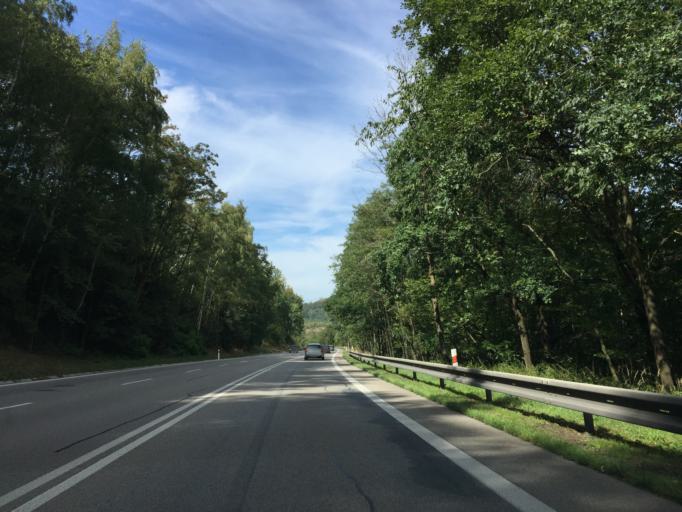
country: CZ
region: Central Bohemia
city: Votice
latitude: 49.6266
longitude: 14.6509
